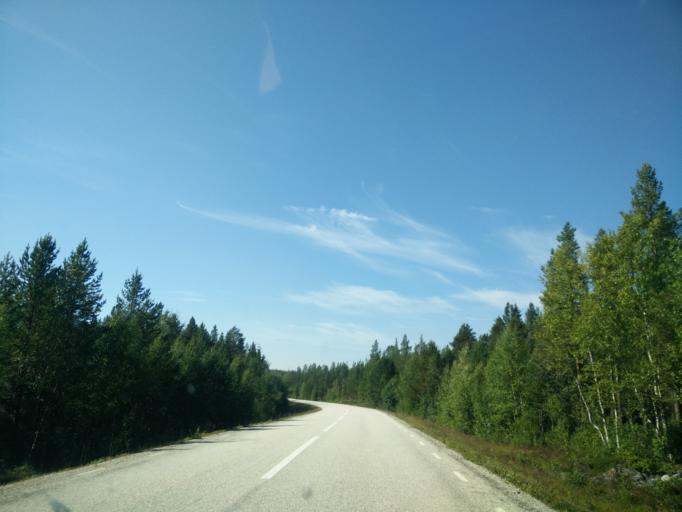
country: SE
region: Jaemtland
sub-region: Are Kommun
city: Jarpen
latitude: 62.8282
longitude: 13.4624
